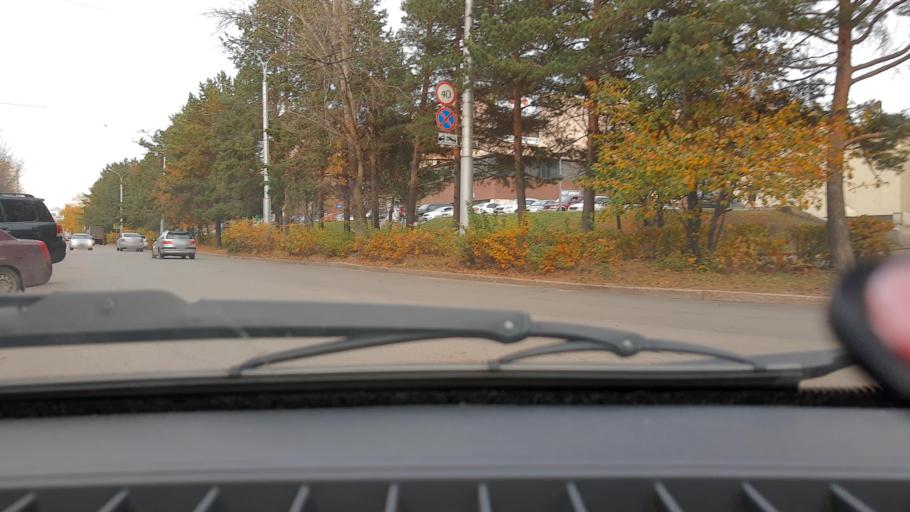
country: RU
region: Bashkortostan
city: Ufa
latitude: 54.7404
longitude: 56.0250
